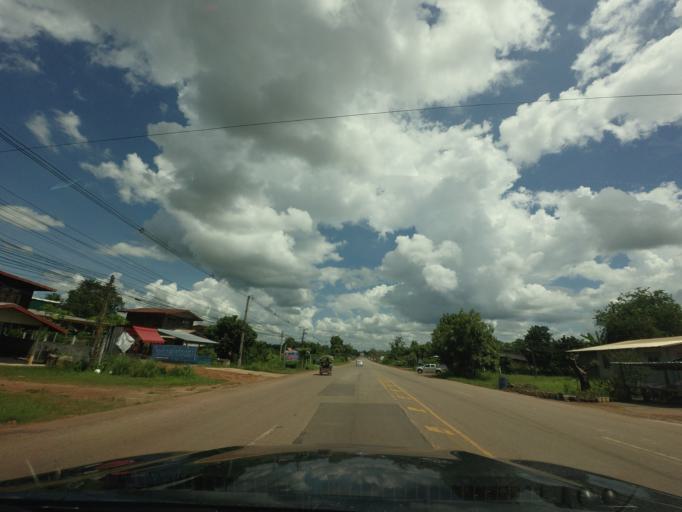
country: TH
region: Changwat Udon Thani
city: Ban Dung
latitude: 17.6793
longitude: 103.2372
